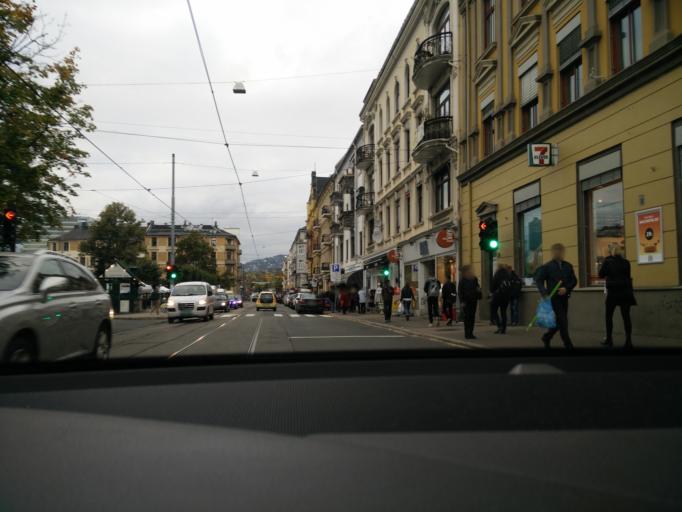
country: NO
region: Oslo
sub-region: Oslo
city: Oslo
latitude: 59.9280
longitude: 10.7191
